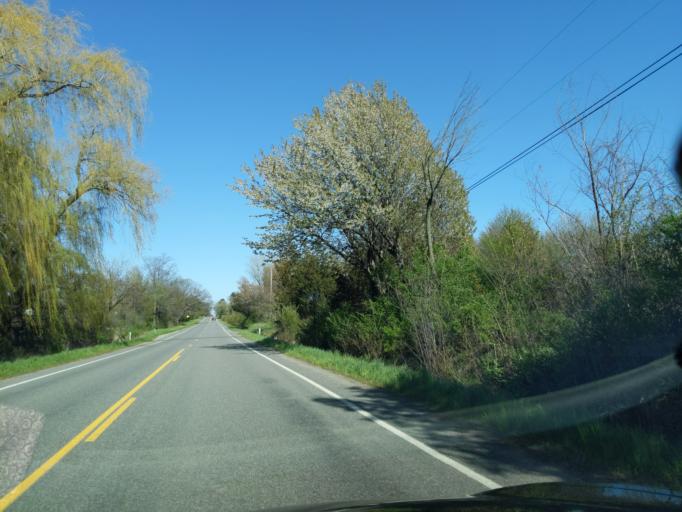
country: US
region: Michigan
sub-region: Kent County
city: Forest Hills
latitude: 42.8852
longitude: -85.4413
